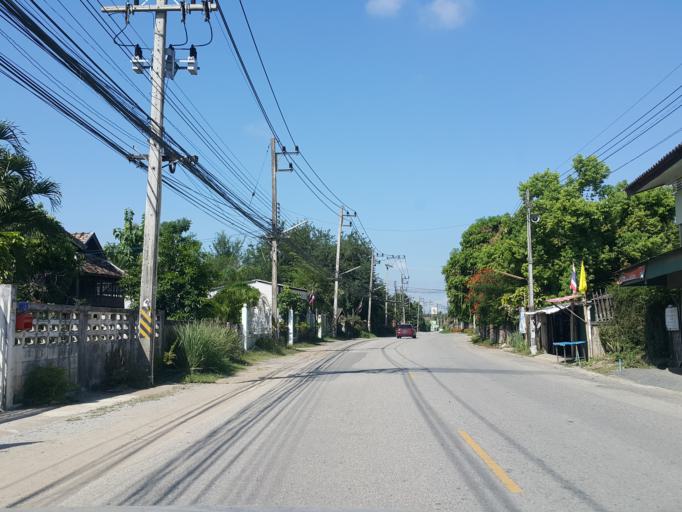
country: TH
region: Chiang Mai
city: San Kamphaeng
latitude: 18.7371
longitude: 99.1451
